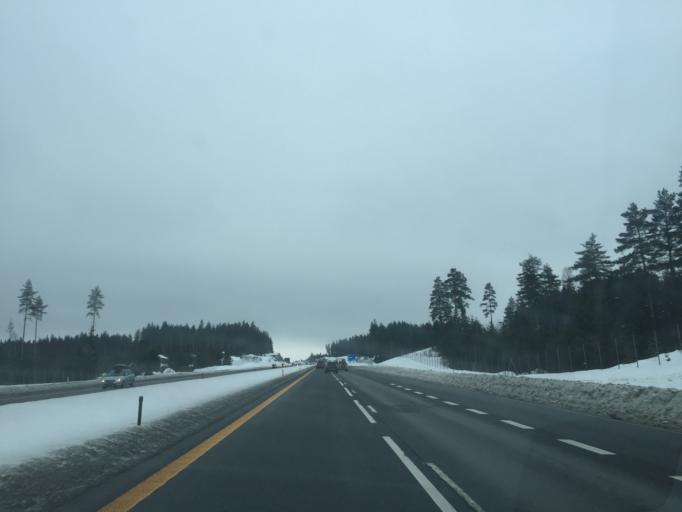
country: NO
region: Hedmark
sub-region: Stange
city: Stange
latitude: 60.6807
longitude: 11.2848
